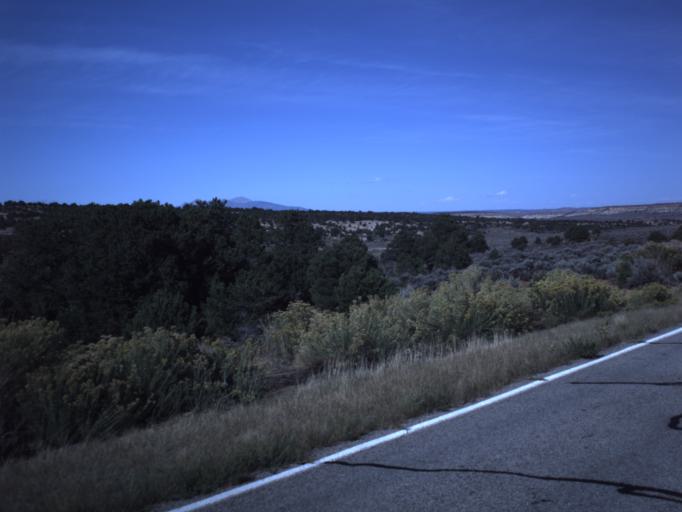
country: US
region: Utah
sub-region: San Juan County
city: Monticello
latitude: 37.9982
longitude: -109.4721
